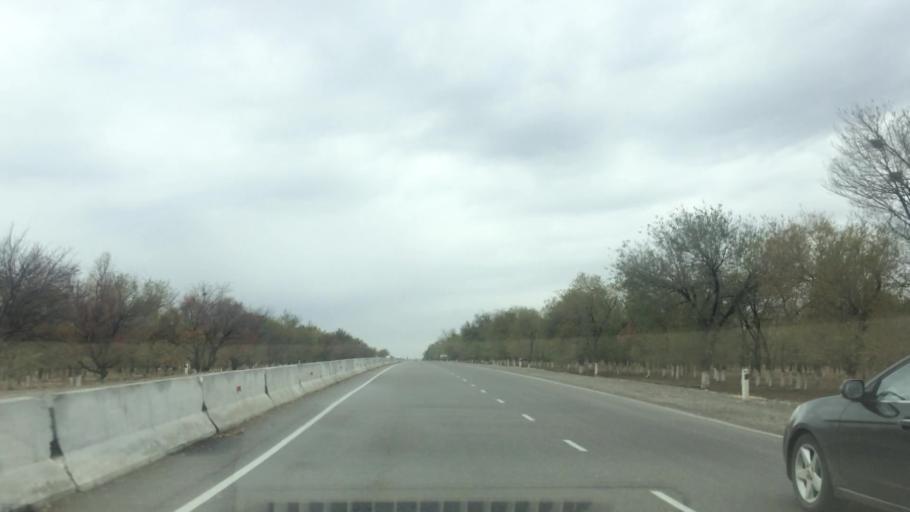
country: UZ
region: Samarqand
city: Bulung'ur
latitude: 39.9176
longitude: 67.5144
